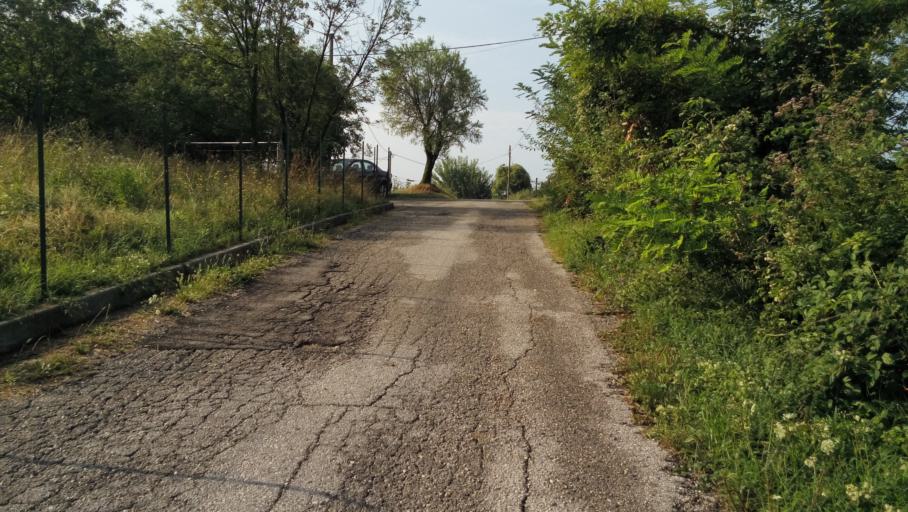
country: IT
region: Veneto
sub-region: Provincia di Vicenza
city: Monteviale
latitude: 45.5436
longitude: 11.4565
